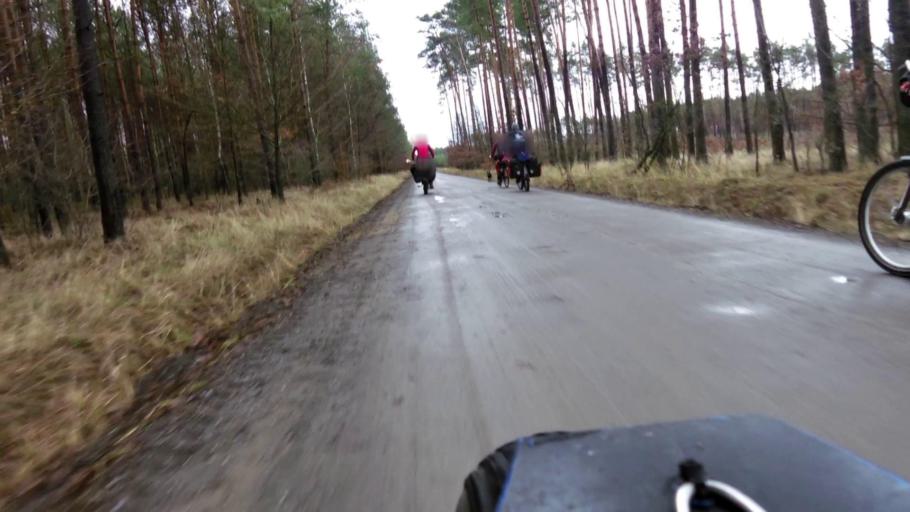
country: PL
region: Lubusz
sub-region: Powiat gorzowski
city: Witnica
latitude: 52.7013
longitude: 14.8355
